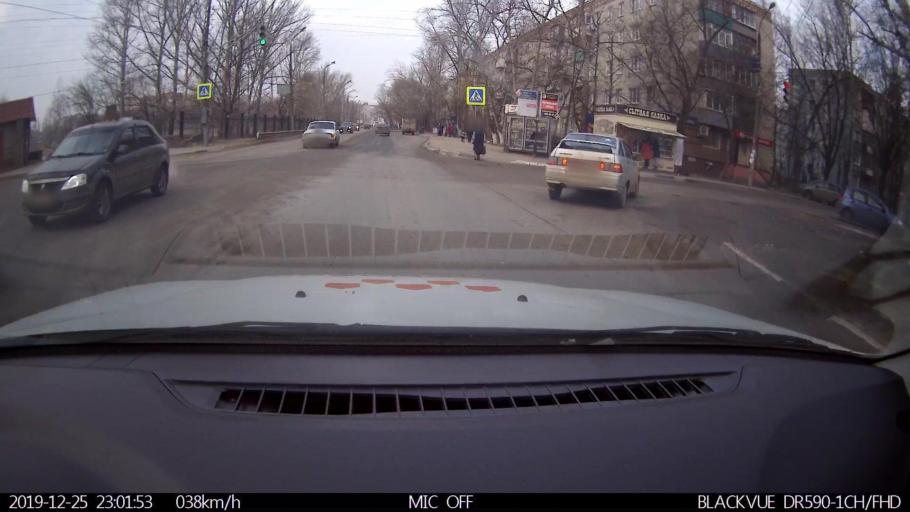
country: RU
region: Nizjnij Novgorod
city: Gorbatovka
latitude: 56.3567
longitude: 43.8349
